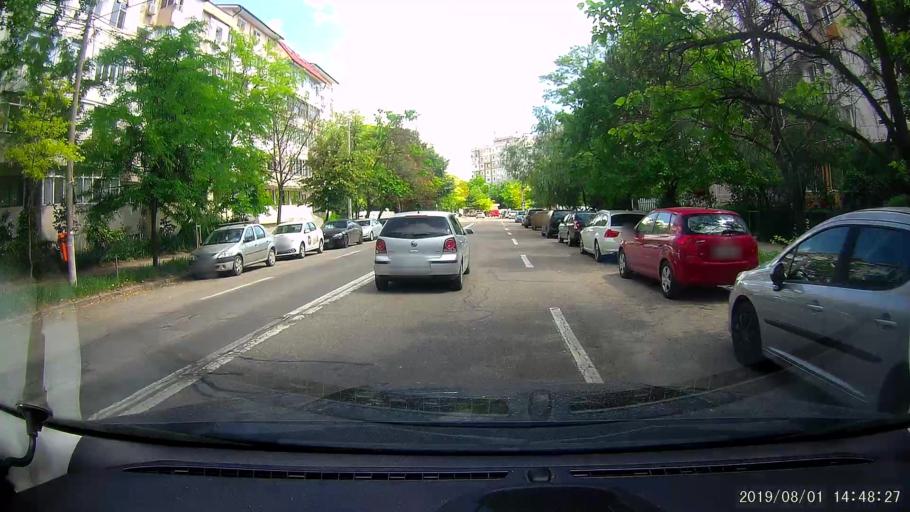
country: RO
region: Galati
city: Galati
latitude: 45.4105
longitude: 28.0091
